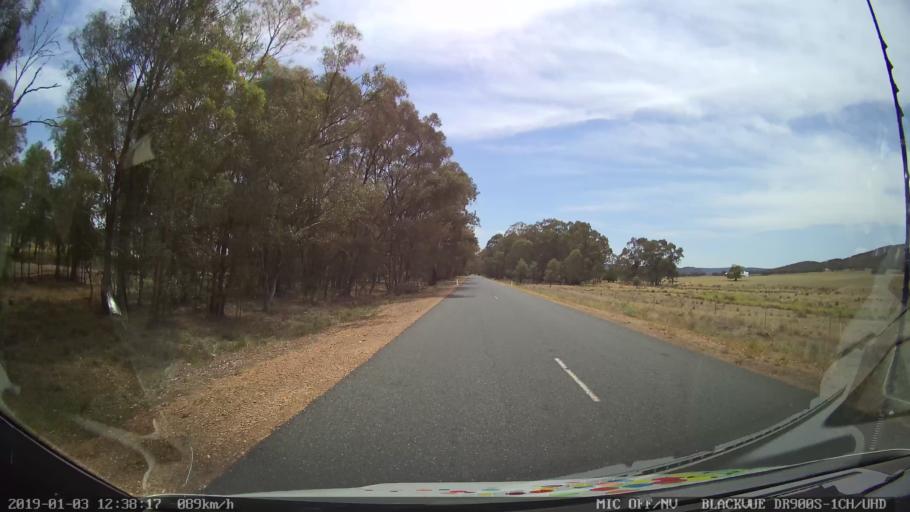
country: AU
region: New South Wales
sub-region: Weddin
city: Grenfell
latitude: -33.8346
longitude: 148.1937
